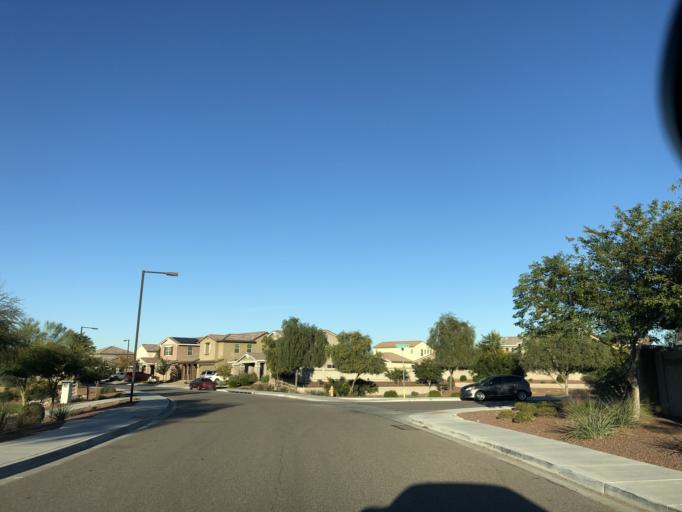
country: US
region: Arizona
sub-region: Maricopa County
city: Sun City West
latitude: 33.7211
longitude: -112.3227
